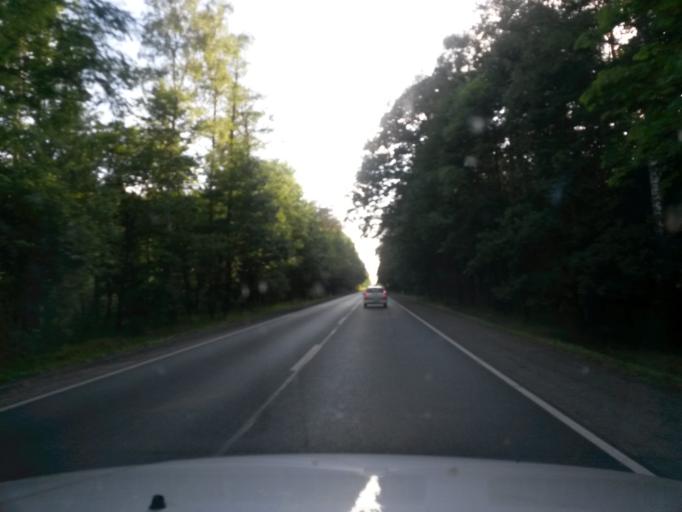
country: PL
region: Lodz Voivodeship
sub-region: Powiat belchatowski
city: Kluki
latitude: 51.3384
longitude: 19.1899
